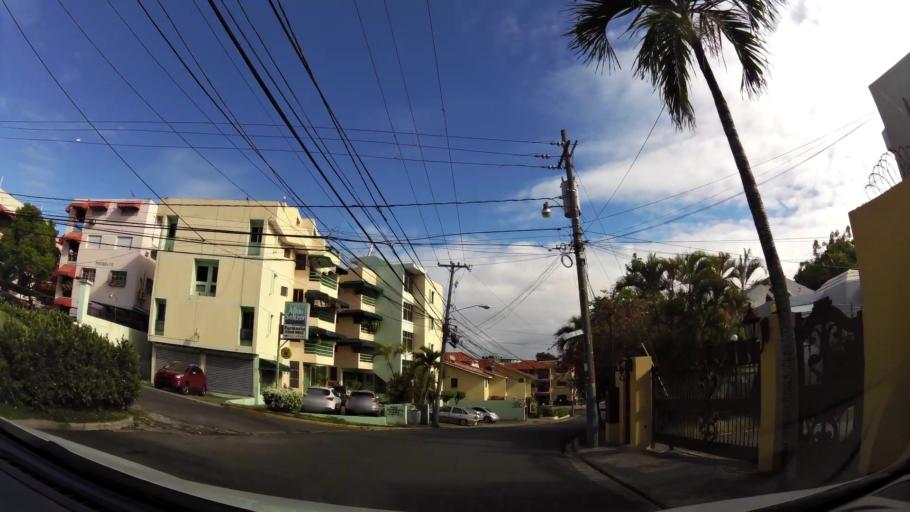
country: DO
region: Nacional
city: La Julia
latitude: 18.4747
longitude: -69.9472
